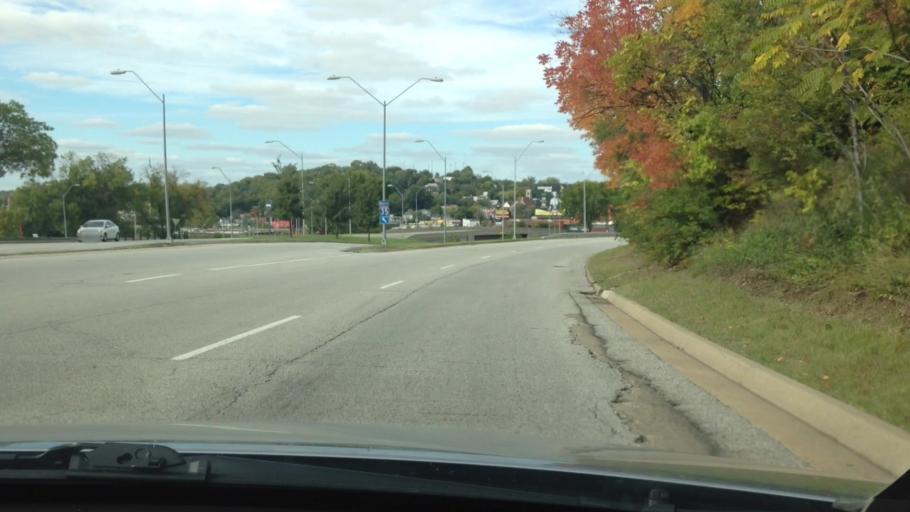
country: US
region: Missouri
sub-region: Jackson County
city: Kansas City
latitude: 39.0777
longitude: -94.5913
